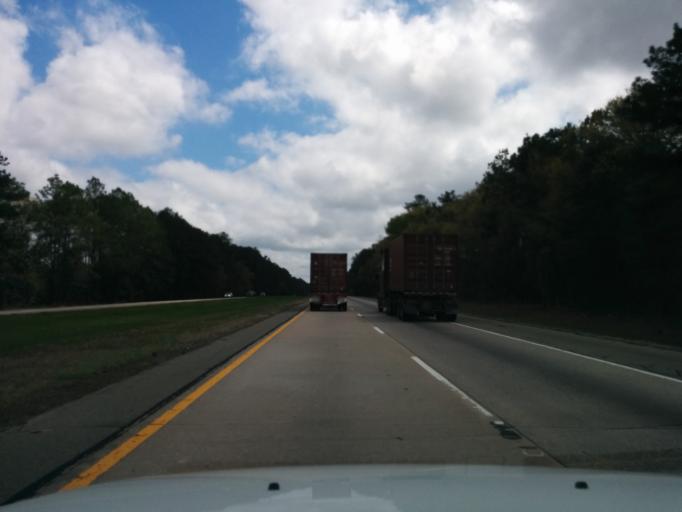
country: US
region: Georgia
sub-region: Bryan County
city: Pembroke
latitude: 32.1953
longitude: -81.4789
